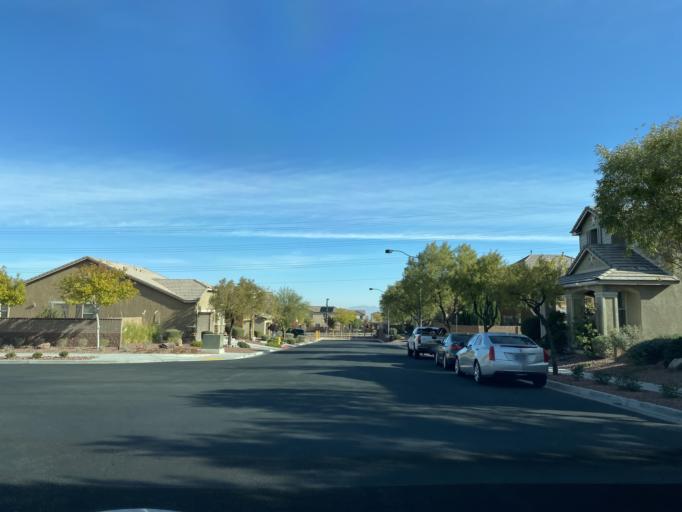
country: US
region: Nevada
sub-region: Clark County
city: Summerlin South
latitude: 36.2987
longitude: -115.3304
